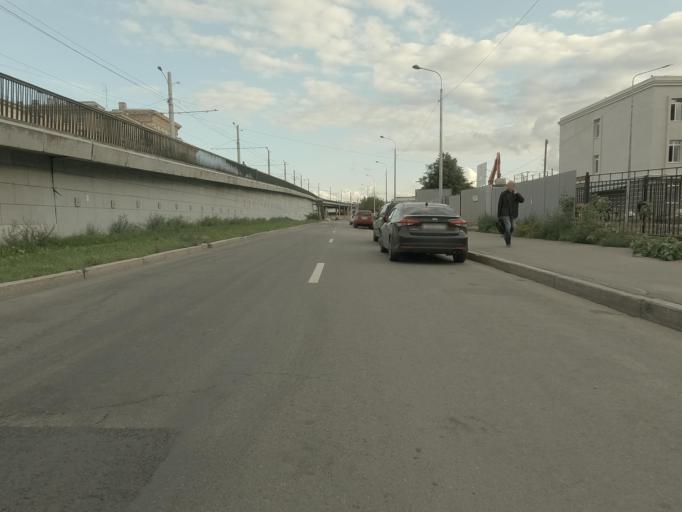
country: RU
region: St.-Petersburg
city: Avtovo
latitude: 59.8669
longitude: 30.2572
